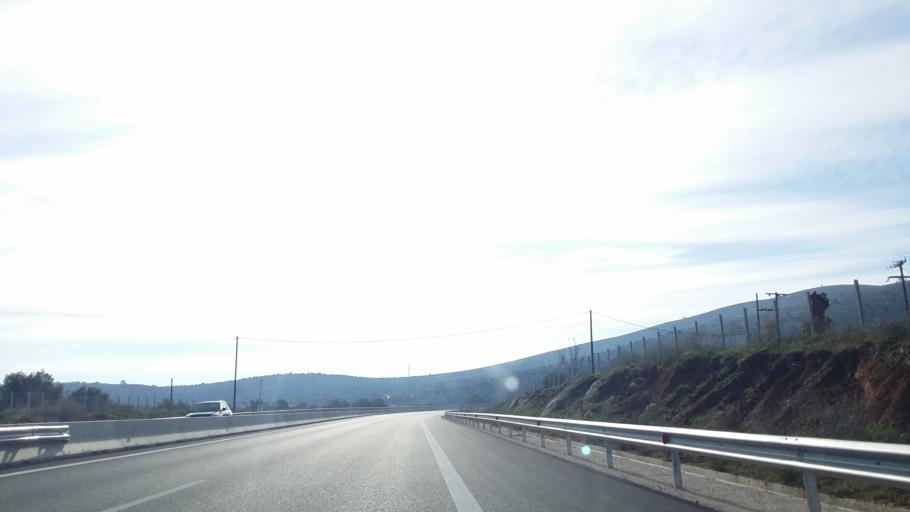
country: GR
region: West Greece
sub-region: Nomos Aitolias kai Akarnanias
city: Sardinia
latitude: 38.8736
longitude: 21.1959
